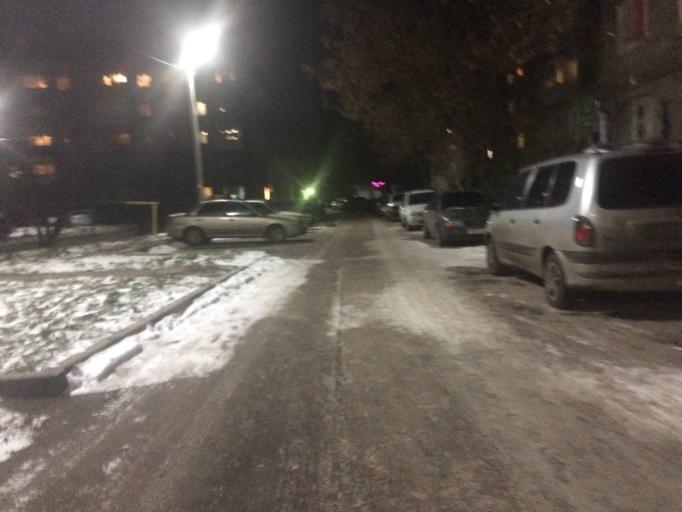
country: RU
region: Rjazan
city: Ryazan'
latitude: 54.6222
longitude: 39.7221
